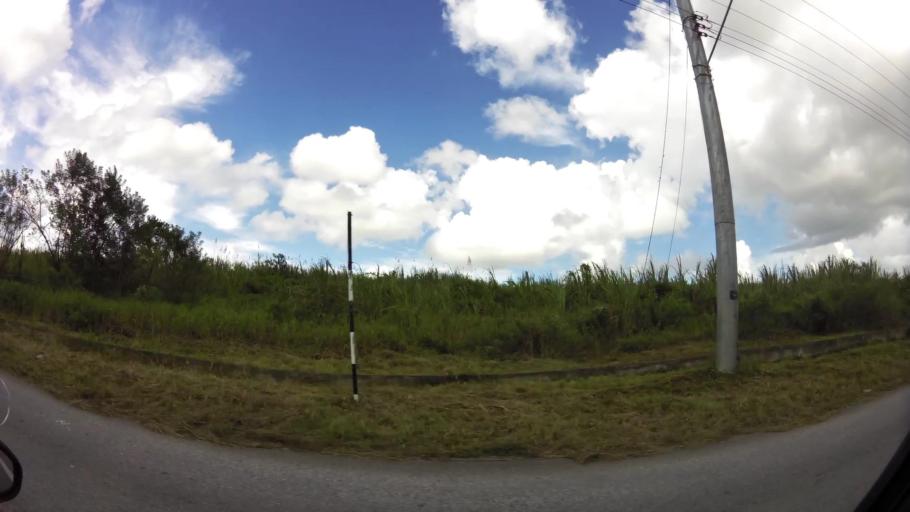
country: TT
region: Penal/Debe
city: Debe
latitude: 10.2357
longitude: -61.4340
